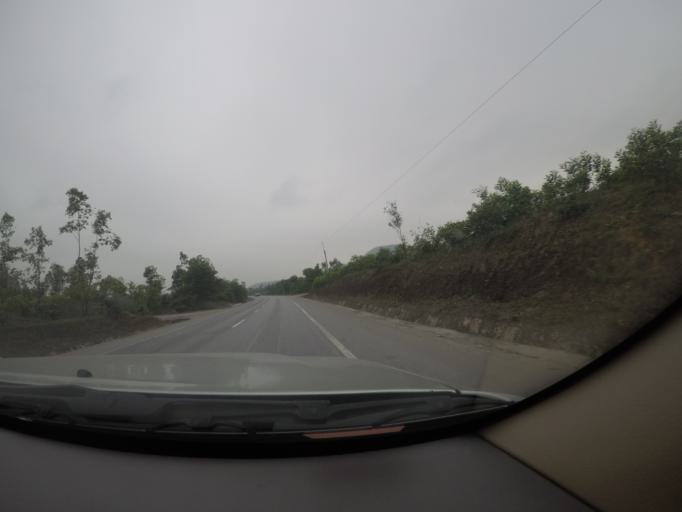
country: VN
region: Ha Tinh
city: Ky Anh
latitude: 18.0286
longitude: 106.3289
